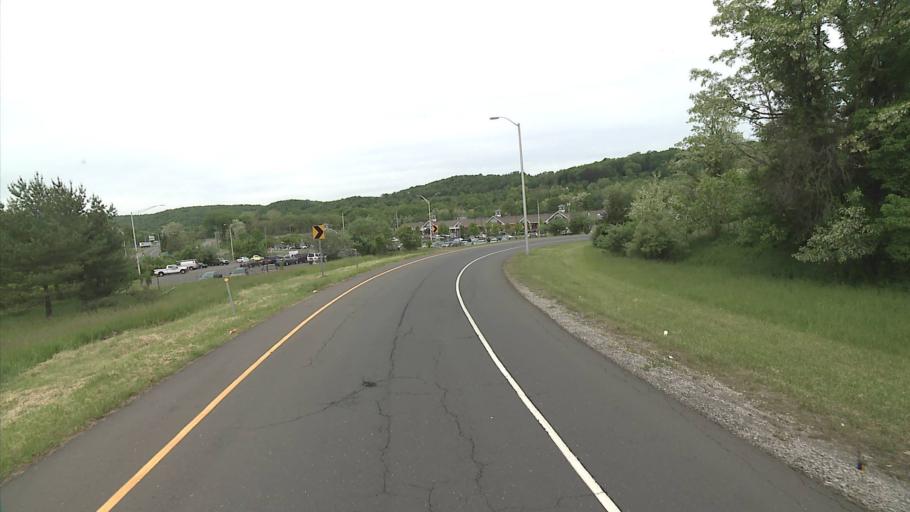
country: US
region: New York
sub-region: Putnam County
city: Peach Lake
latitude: 41.3910
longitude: -73.5196
